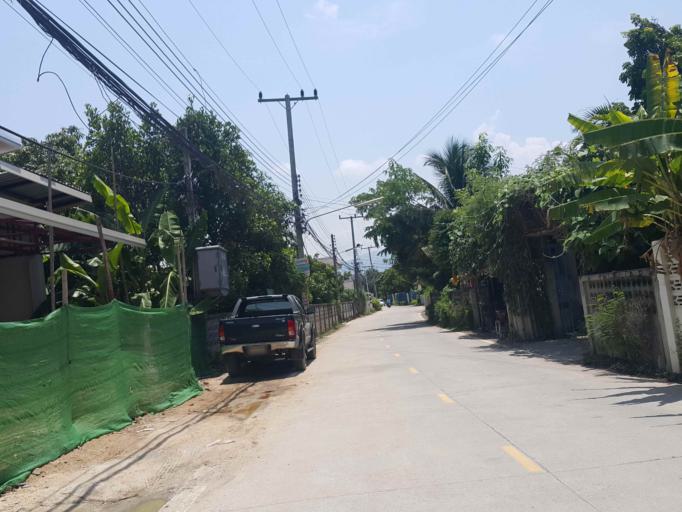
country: TH
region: Chiang Mai
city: San Sai
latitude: 18.8162
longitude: 99.0588
